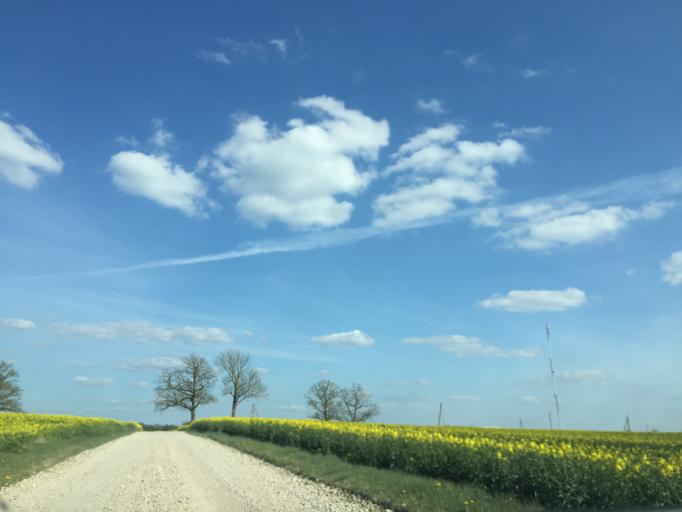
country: LV
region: Bauskas Rajons
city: Bauska
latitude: 56.4885
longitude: 24.3266
